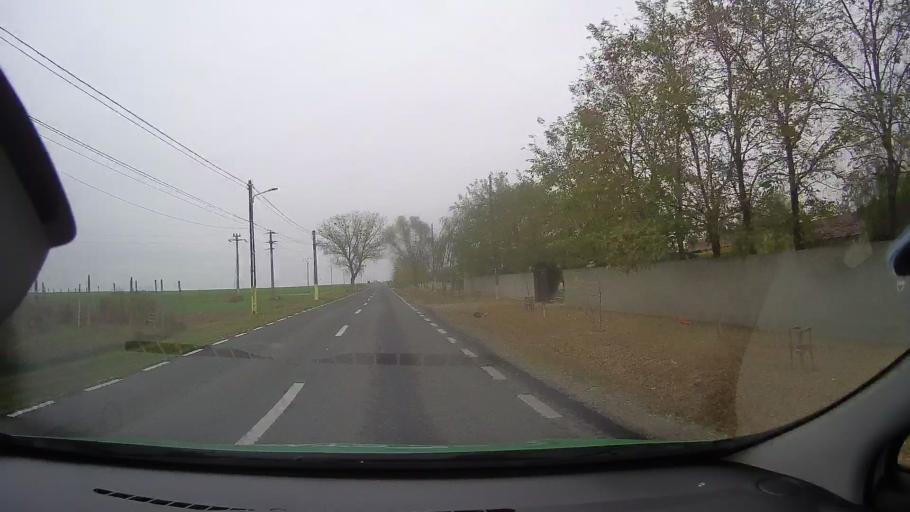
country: RO
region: Constanta
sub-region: Comuna Tortoman
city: Tortoman
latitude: 44.3496
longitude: 28.2178
